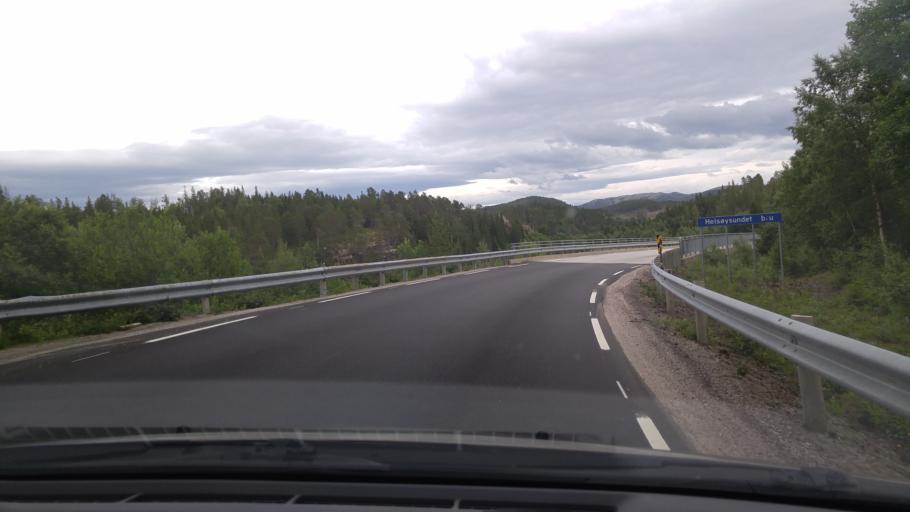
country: NO
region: Nord-Trondelag
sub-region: Namsos
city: Namsos
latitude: 64.5624
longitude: 11.5036
